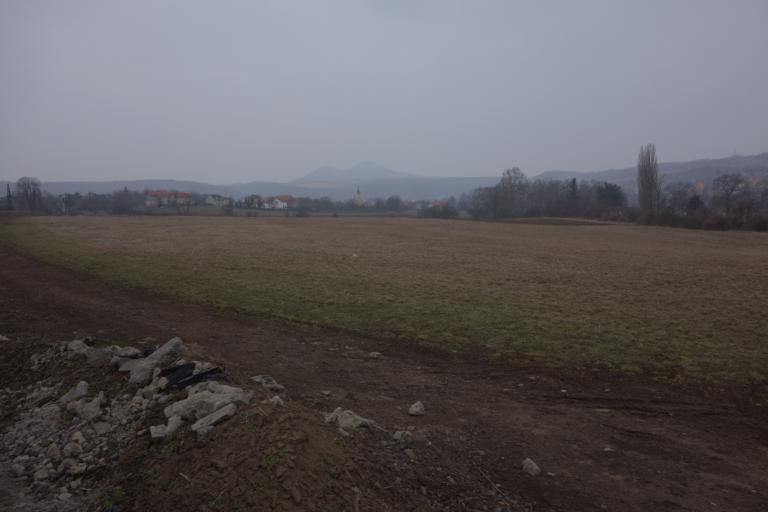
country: CZ
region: Ustecky
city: Lovosice
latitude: 50.5738
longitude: 14.0430
